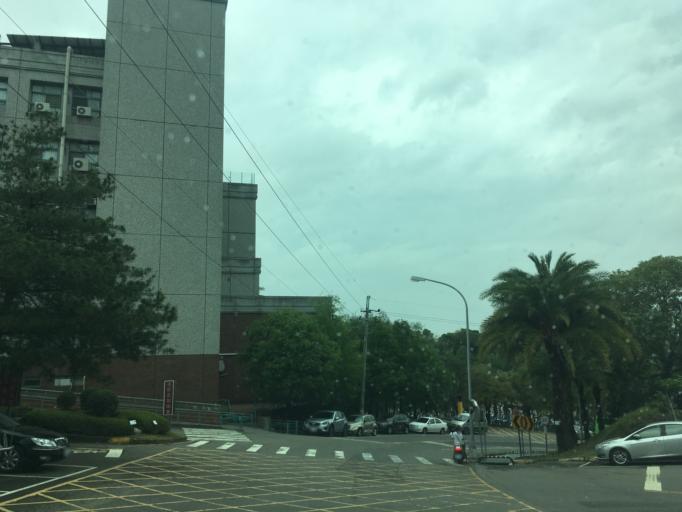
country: TW
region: Taiwan
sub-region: Taichung City
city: Taichung
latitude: 24.0689
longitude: 120.7160
